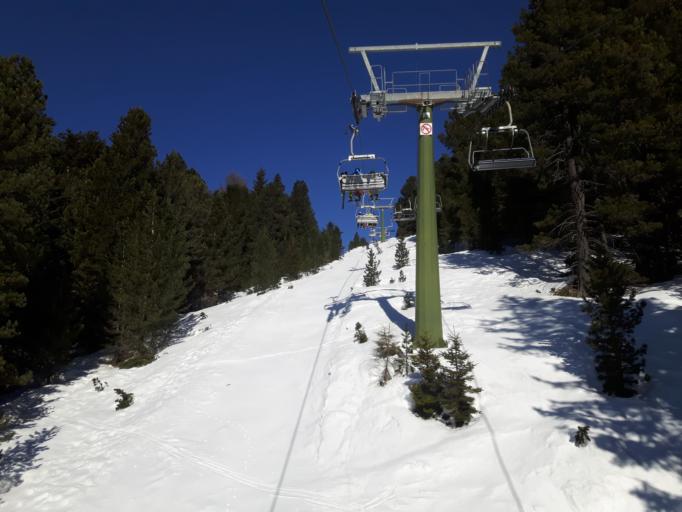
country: IT
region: Trentino-Alto Adige
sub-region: Provincia di Trento
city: Panchia
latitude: 46.3450
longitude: 11.5429
